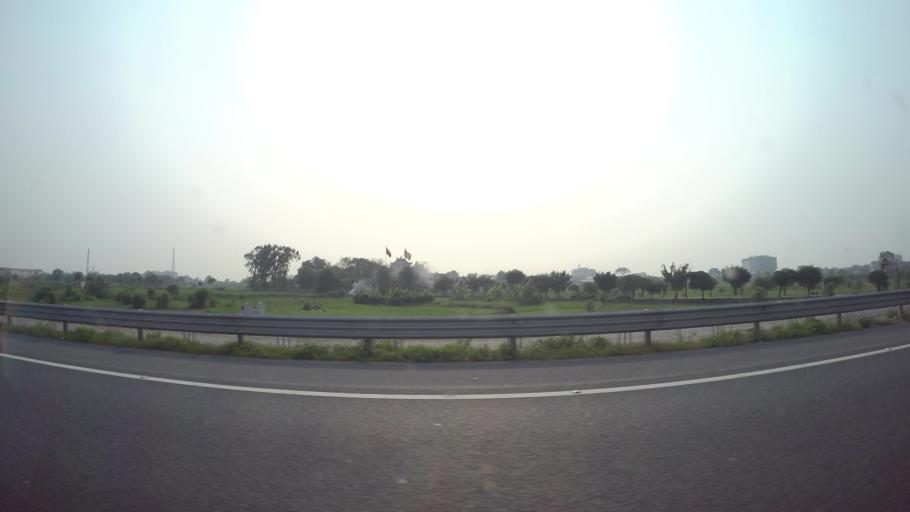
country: VN
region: Ha Noi
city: Van Dien
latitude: 20.9163
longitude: 105.8598
